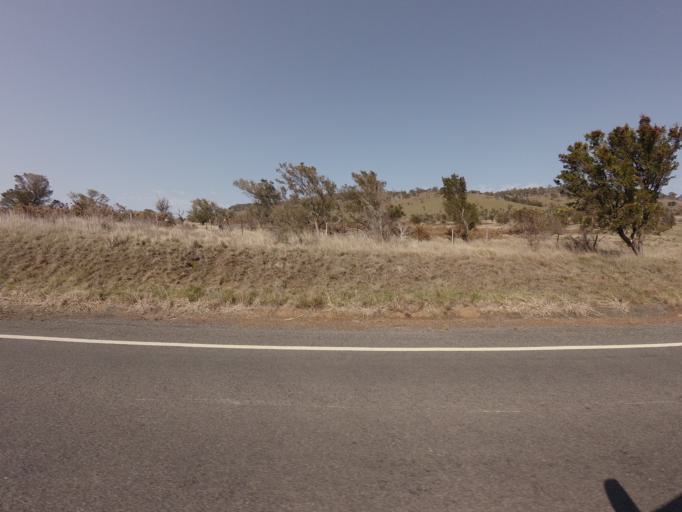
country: AU
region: Tasmania
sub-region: Northern Midlands
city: Evandale
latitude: -41.8146
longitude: 147.5574
